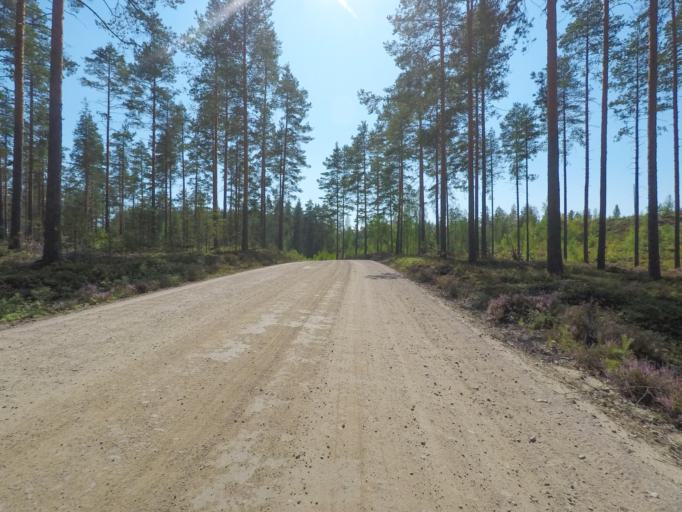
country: FI
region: Southern Savonia
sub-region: Mikkeli
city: Puumala
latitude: 61.4186
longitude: 28.0419
